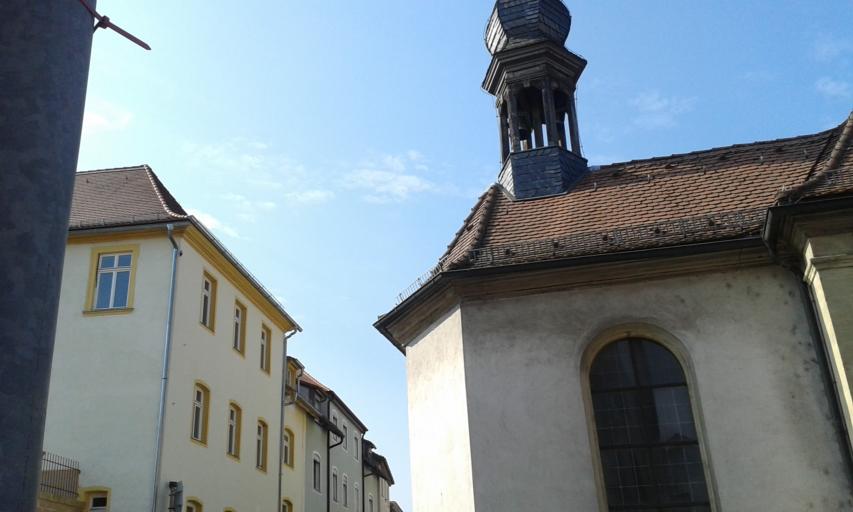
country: DE
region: Bavaria
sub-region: Upper Franconia
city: Bischberg
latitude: 49.9047
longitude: 10.8562
